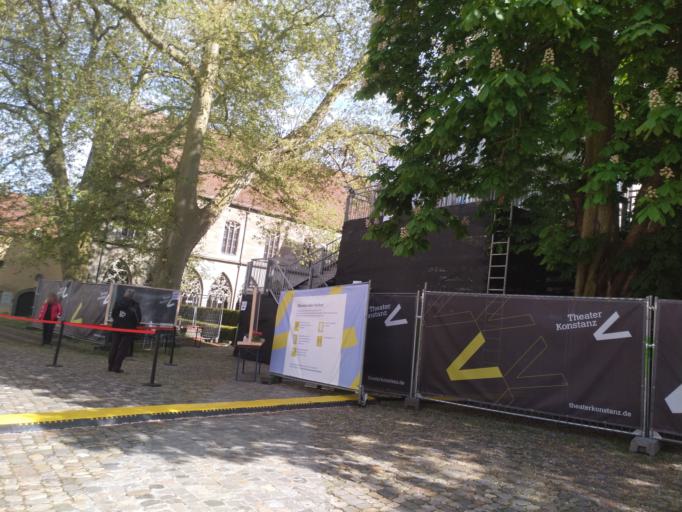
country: DE
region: Baden-Wuerttemberg
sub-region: Freiburg Region
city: Konstanz
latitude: 47.6638
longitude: 9.1761
